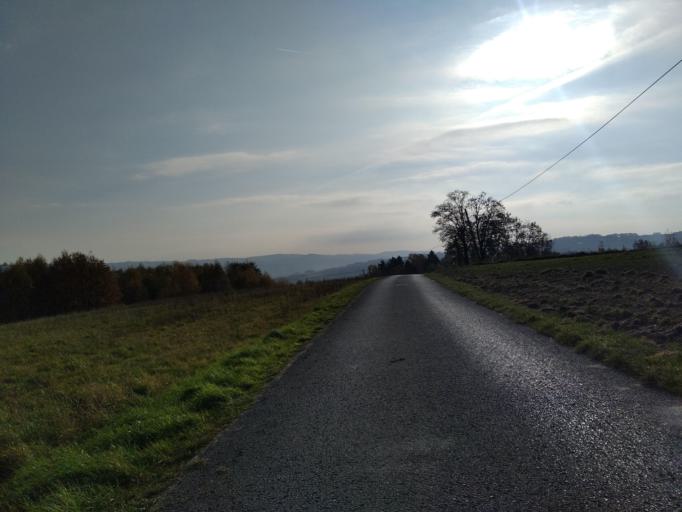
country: PL
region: Subcarpathian Voivodeship
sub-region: Powiat strzyzowski
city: Babica
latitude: 49.9037
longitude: 21.8556
